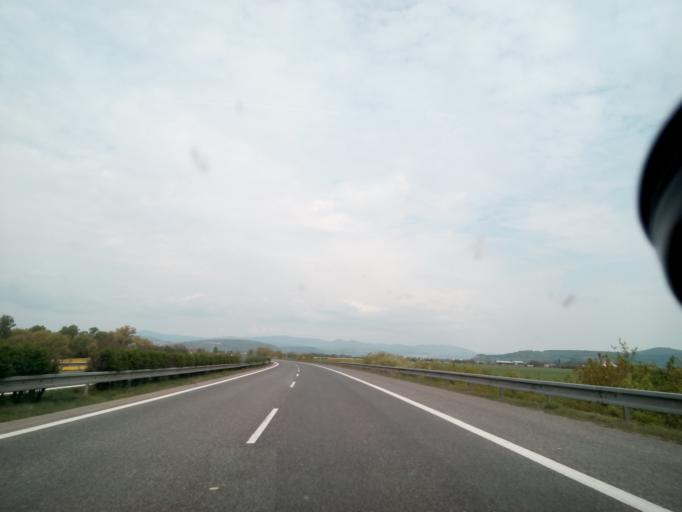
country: SK
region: Trenciansky
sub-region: Okres Nove Mesto nad Vahom
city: Nove Mesto nad Vahom
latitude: 48.7210
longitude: 17.8746
